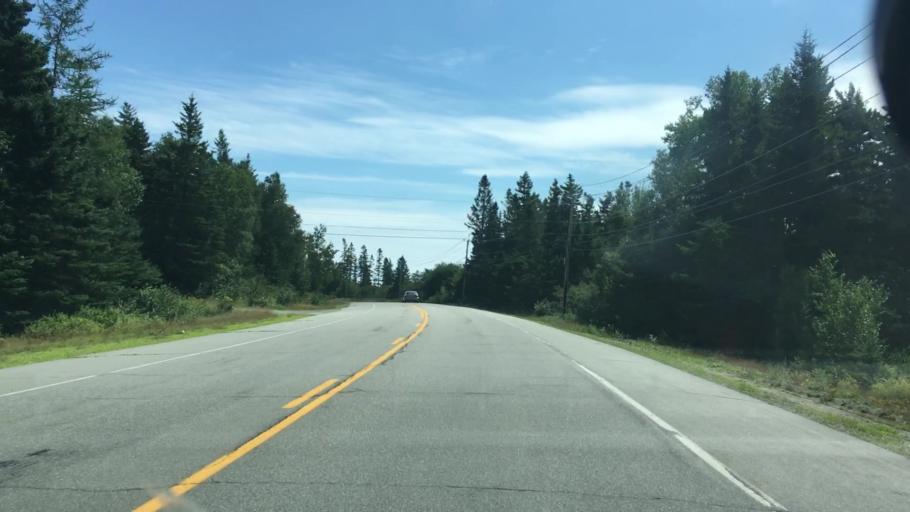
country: US
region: Maine
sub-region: Washington County
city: Eastport
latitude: 44.9434
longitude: -67.0389
